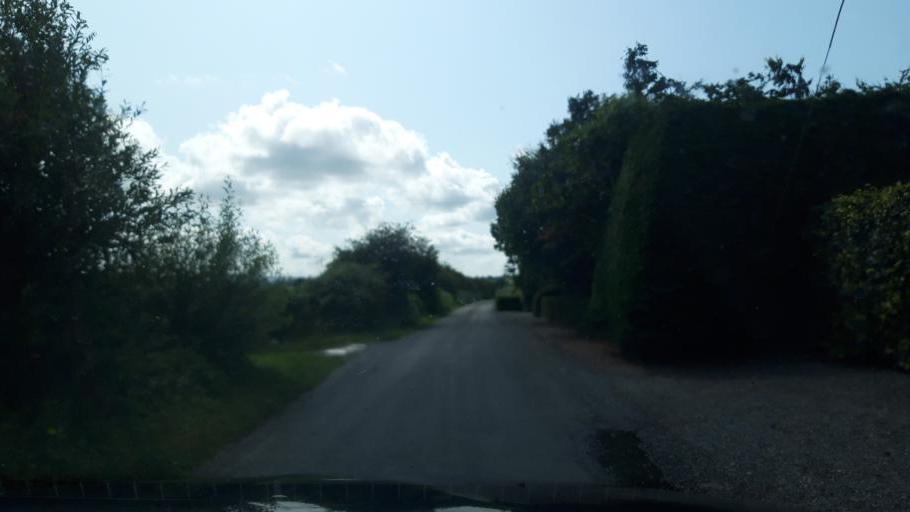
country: IE
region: Leinster
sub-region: Kilkenny
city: Graiguenamanagh
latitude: 52.5869
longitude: -6.9965
